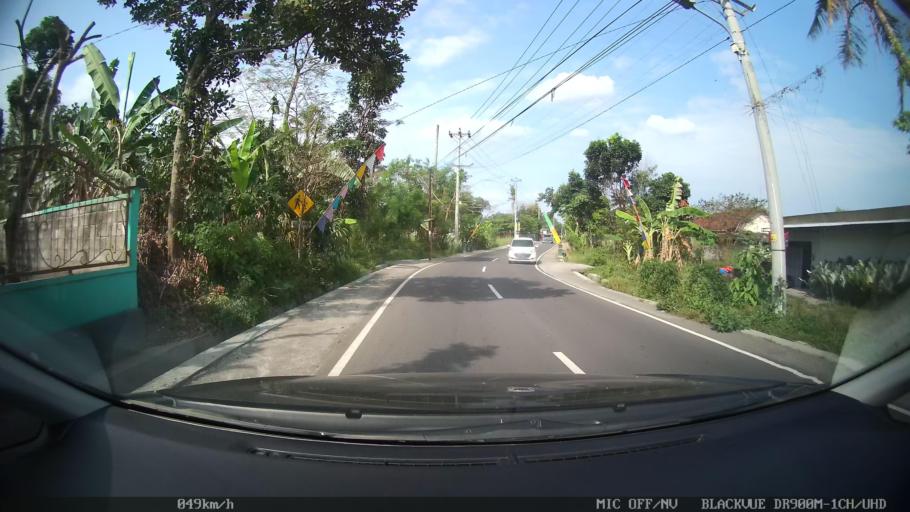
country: ID
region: Daerah Istimewa Yogyakarta
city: Depok
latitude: -7.7277
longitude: 110.4247
